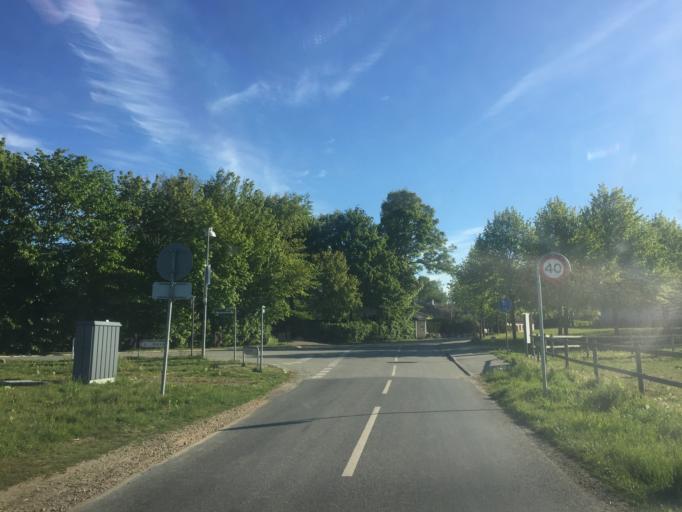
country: DK
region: Capital Region
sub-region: Egedal Kommune
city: Smorumnedre
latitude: 55.7341
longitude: 12.2679
